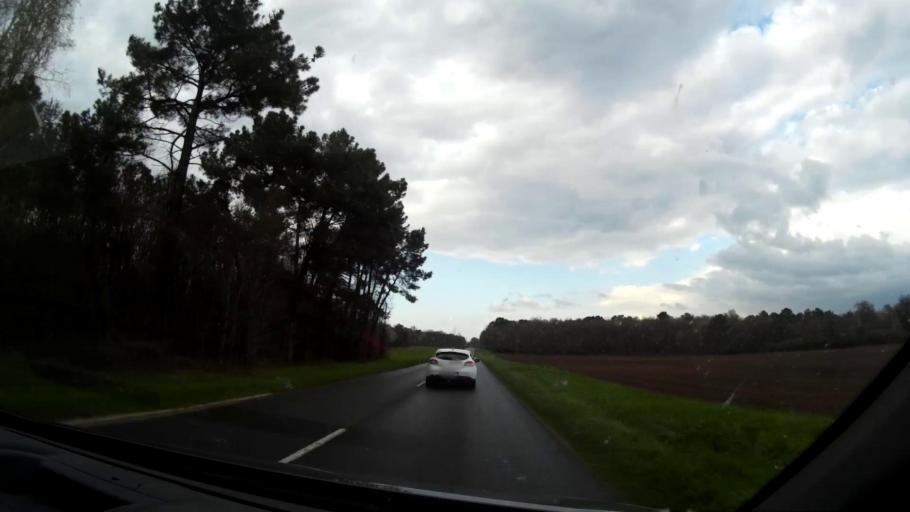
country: FR
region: Centre
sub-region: Departement du Loir-et-Cher
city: Cormeray
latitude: 47.4575
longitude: 1.4254
